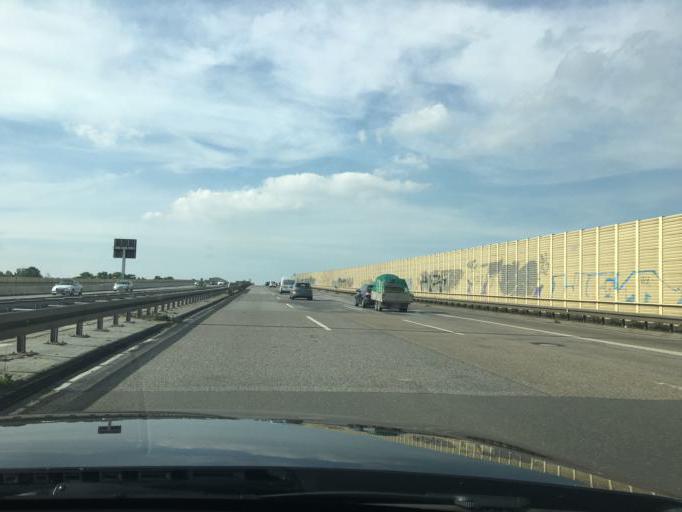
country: DE
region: North Rhine-Westphalia
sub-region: Regierungsbezirk Dusseldorf
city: Hochfeld
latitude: 51.4088
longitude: 6.7716
